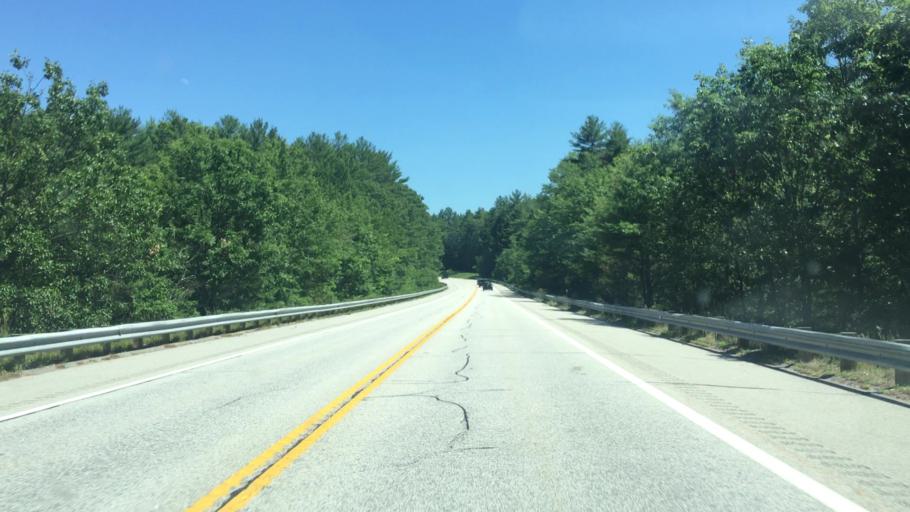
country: US
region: New Hampshire
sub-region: Merrimack County
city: Contoocook
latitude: 43.1785
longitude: -71.7305
